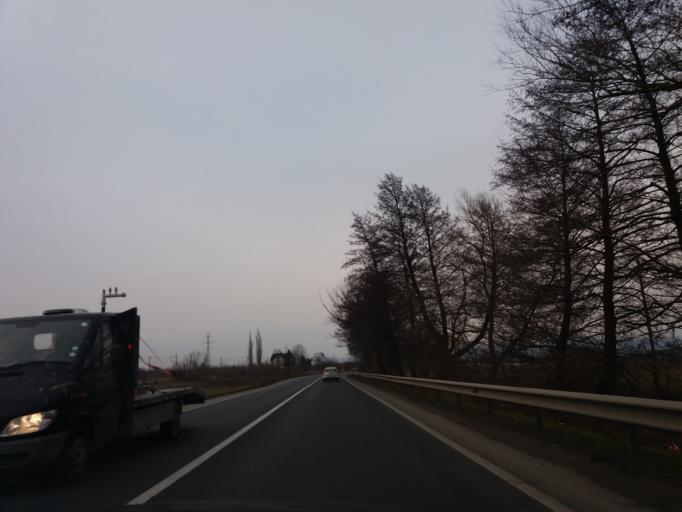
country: RO
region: Hunedoara
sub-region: Comuna Bacia
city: Bacia
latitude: 45.7891
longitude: 23.0016
